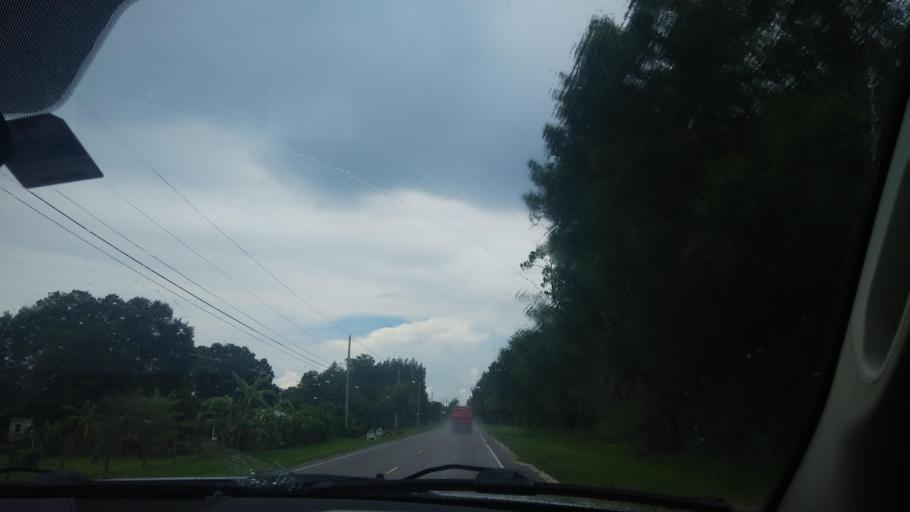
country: US
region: Florida
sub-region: Indian River County
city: Fellsmere
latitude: 27.7902
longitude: -80.6076
